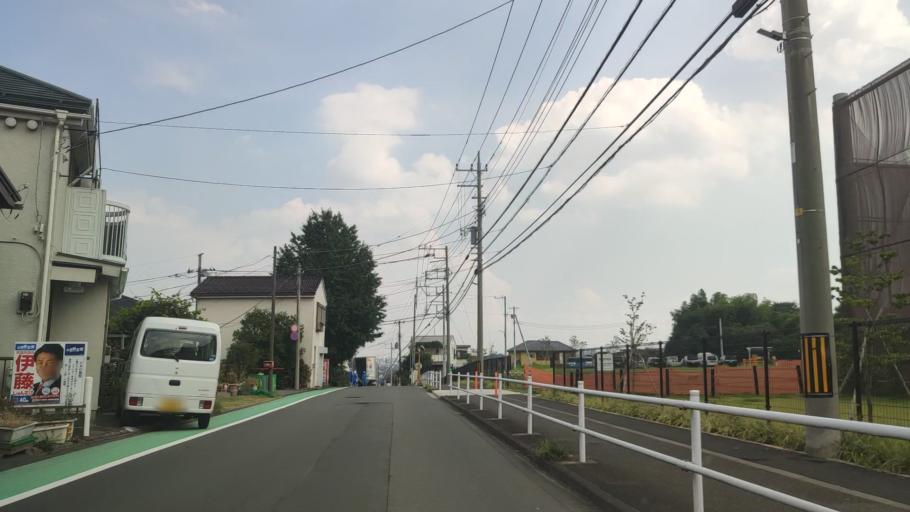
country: JP
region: Tokyo
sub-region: Machida-shi
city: Machida
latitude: 35.5472
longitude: 139.4559
